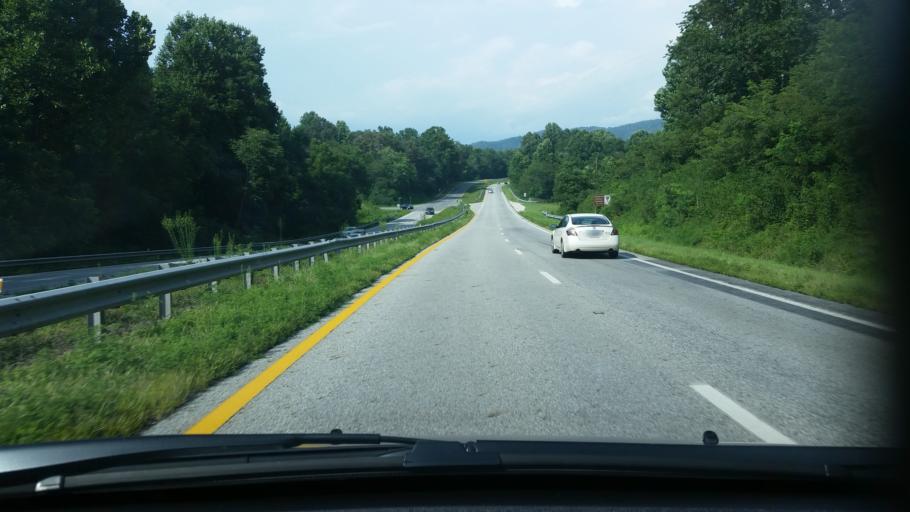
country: US
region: Virginia
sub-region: Nelson County
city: Lovingston
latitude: 37.7392
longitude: -78.8906
